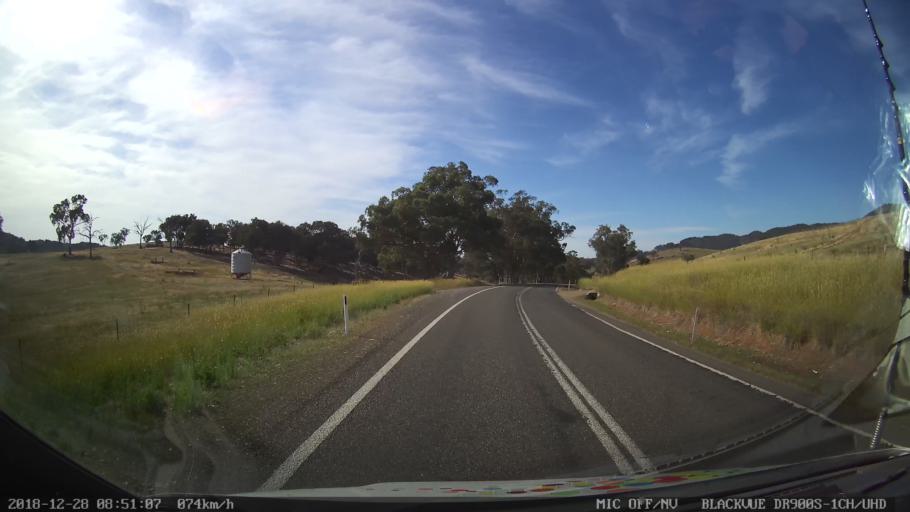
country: AU
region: New South Wales
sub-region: Upper Lachlan Shire
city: Crookwell
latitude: -34.0646
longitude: 149.3394
